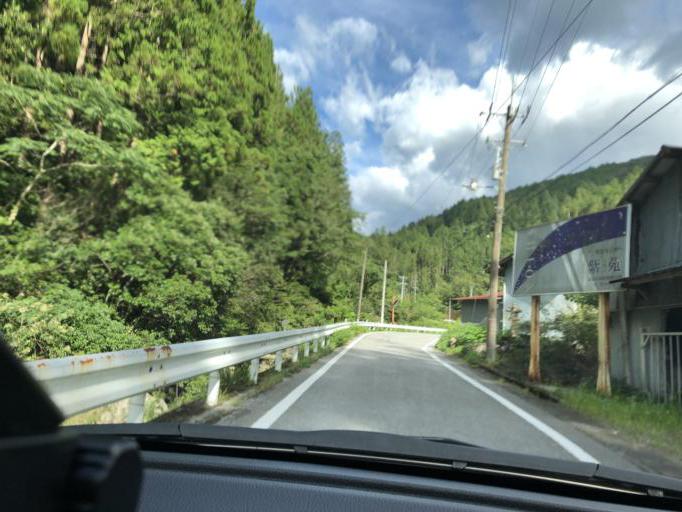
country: JP
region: Kochi
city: Kochi-shi
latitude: 33.6112
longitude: 133.5015
